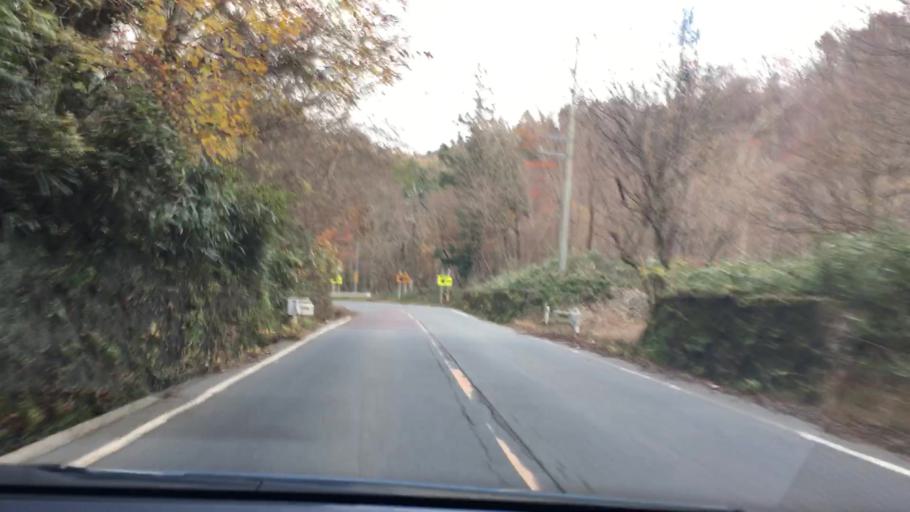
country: JP
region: Yamanashi
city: Otsuki
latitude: 35.4588
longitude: 138.9395
